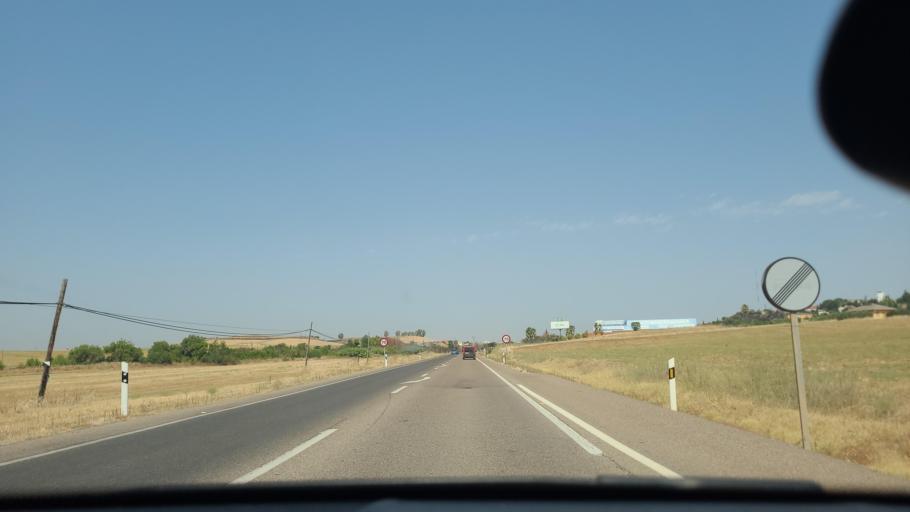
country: ES
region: Extremadura
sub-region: Provincia de Badajoz
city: Badajoz
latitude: 38.8507
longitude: -6.9404
